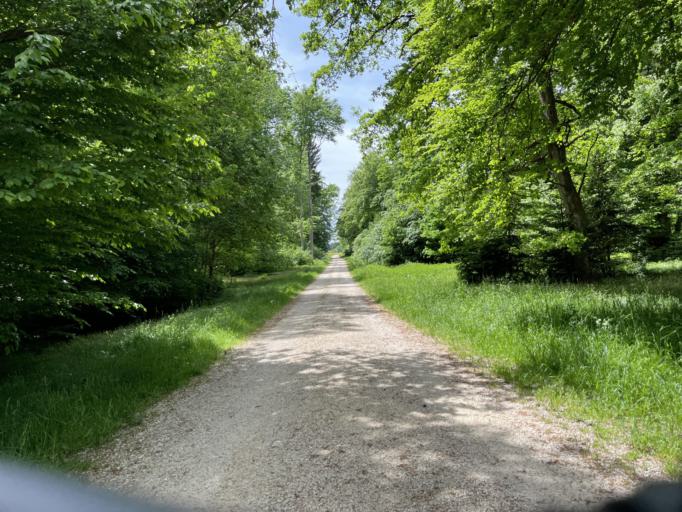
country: DE
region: Baden-Wuerttemberg
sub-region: Tuebingen Region
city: Sigmaringendorf
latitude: 48.0848
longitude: 9.2529
